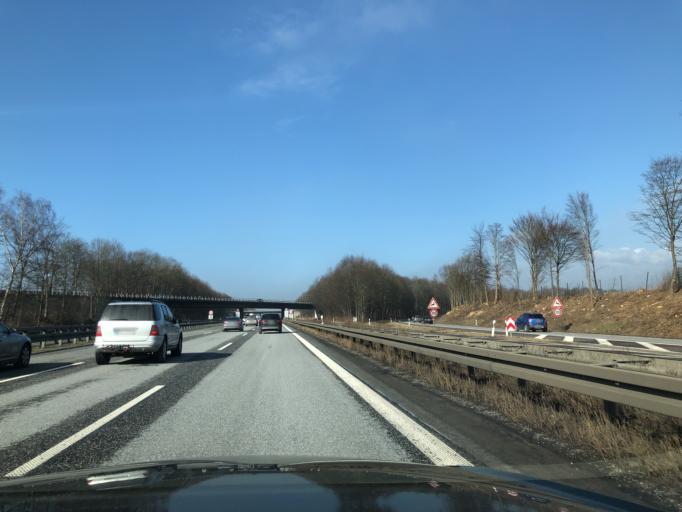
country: DE
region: North Rhine-Westphalia
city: Meckenheim
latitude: 50.5909
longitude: 7.0363
